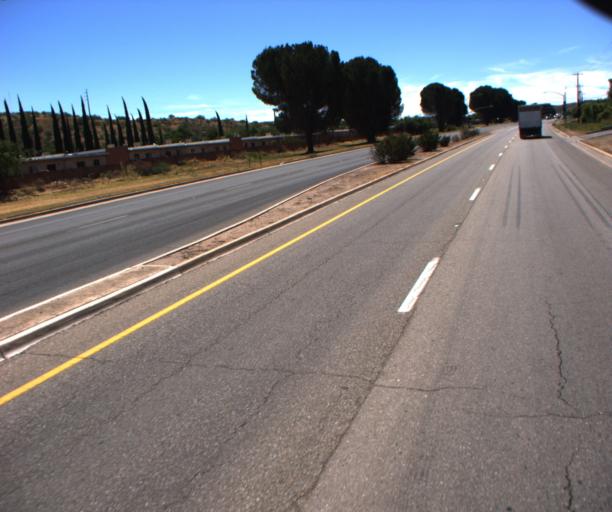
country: US
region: Arizona
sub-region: Santa Cruz County
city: Nogales
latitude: 31.3914
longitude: -110.9539
